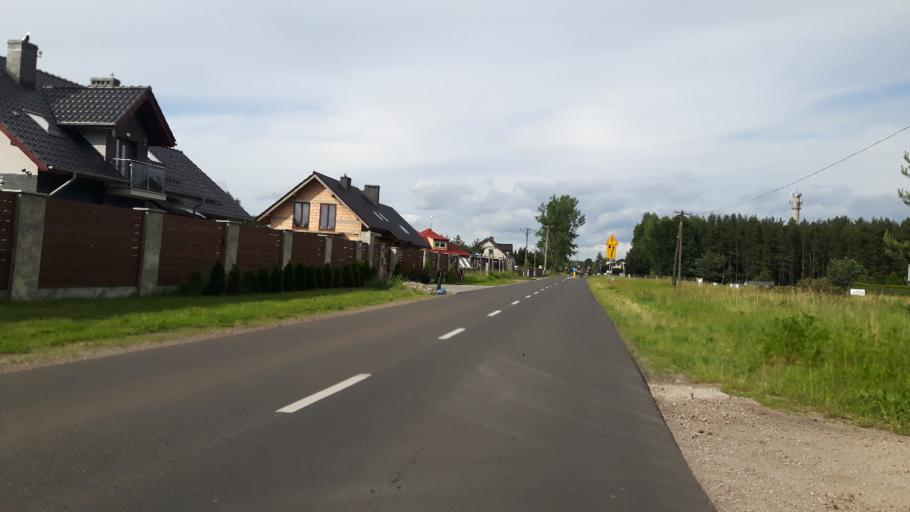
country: PL
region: West Pomeranian Voivodeship
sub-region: Powiat goleniowski
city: Goleniow
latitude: 53.4556
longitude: 14.7664
